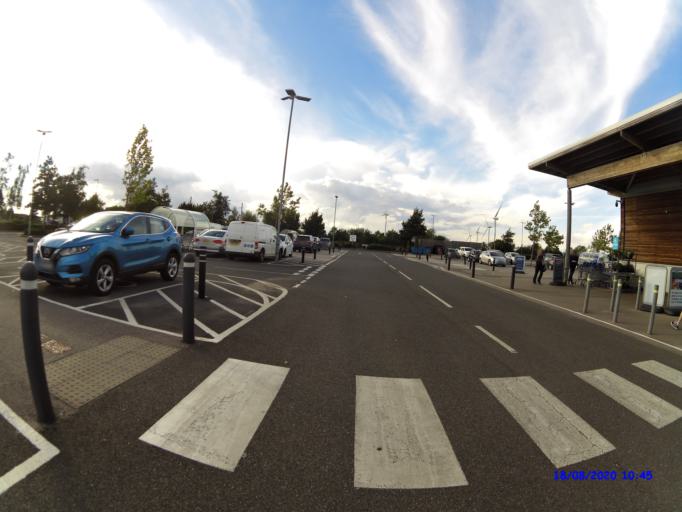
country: GB
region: England
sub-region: Cambridgeshire
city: Ramsey
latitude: 52.4559
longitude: -0.1132
